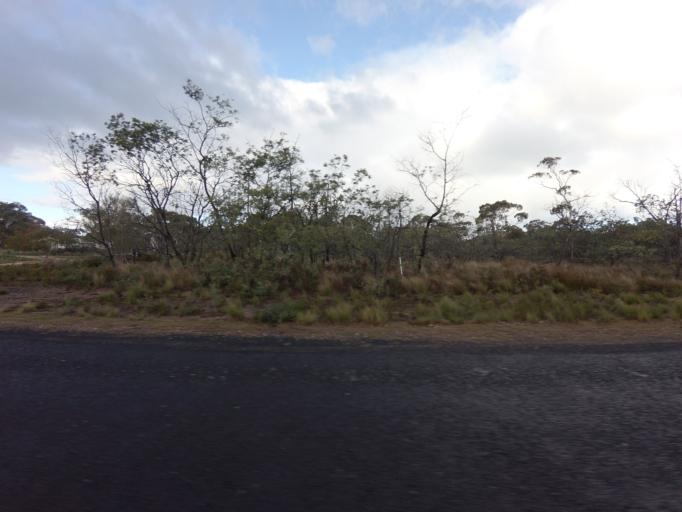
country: AU
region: Tasmania
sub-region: Break O'Day
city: St Helens
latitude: -42.1032
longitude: 148.0726
